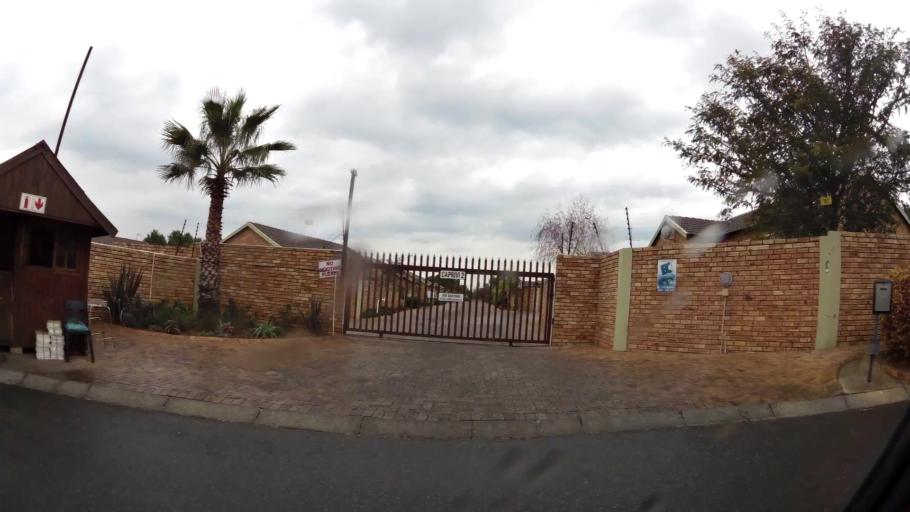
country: ZA
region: Gauteng
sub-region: City of Johannesburg Metropolitan Municipality
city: Roodepoort
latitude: -26.1062
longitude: 27.9175
